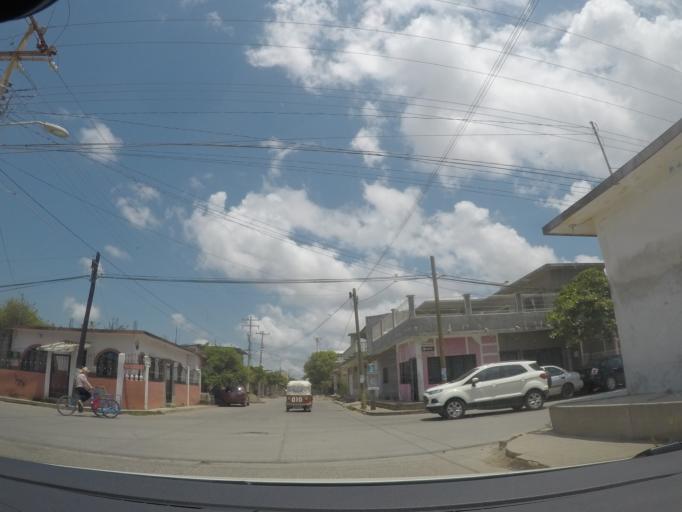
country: MX
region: Oaxaca
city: Juchitan de Zaragoza
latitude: 16.4411
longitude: -95.0133
